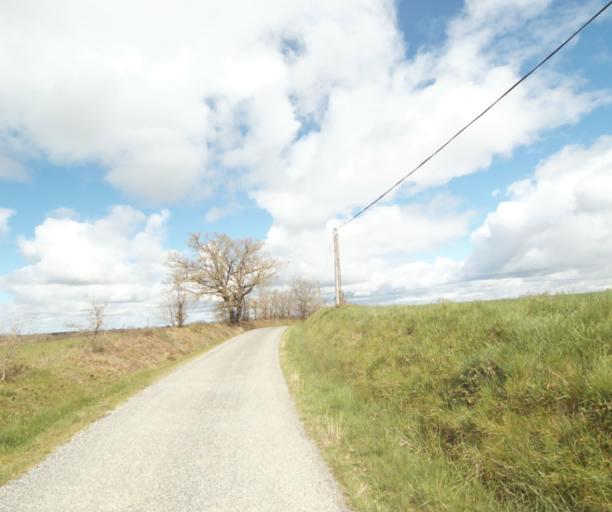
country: FR
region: Midi-Pyrenees
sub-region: Departement de l'Ariege
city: Saverdun
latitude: 43.2080
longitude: 1.5830
